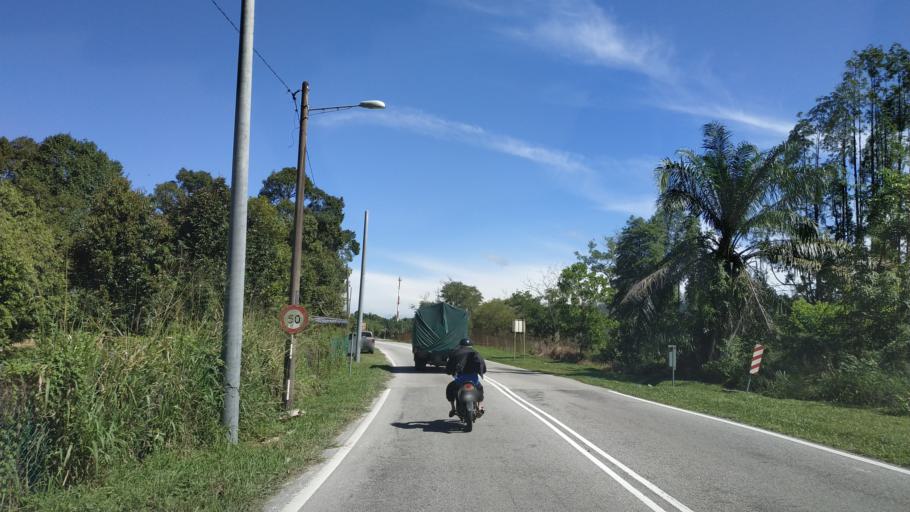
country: MY
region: Kedah
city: Kulim
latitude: 5.3301
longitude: 100.5341
